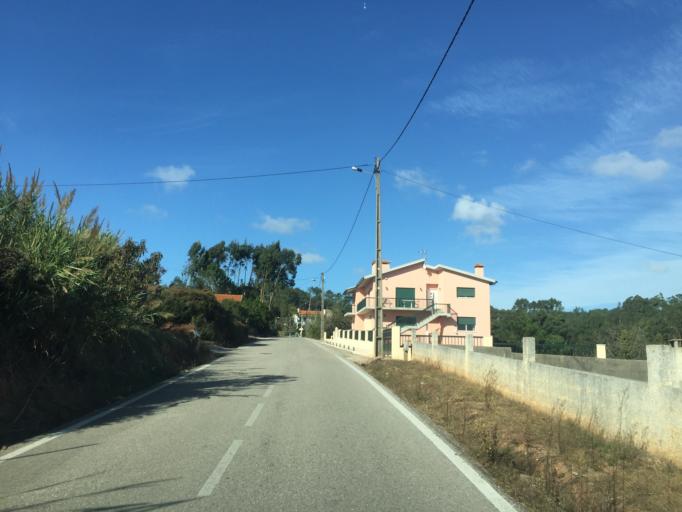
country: PT
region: Coimbra
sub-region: Figueira da Foz
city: Tavarede
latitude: 40.1818
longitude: -8.8376
